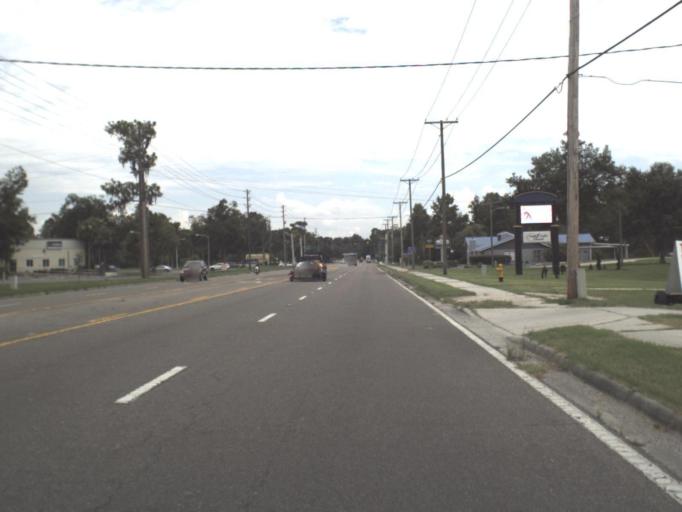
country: US
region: Florida
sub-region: Citrus County
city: Crystal River
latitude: 28.8850
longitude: -82.5434
